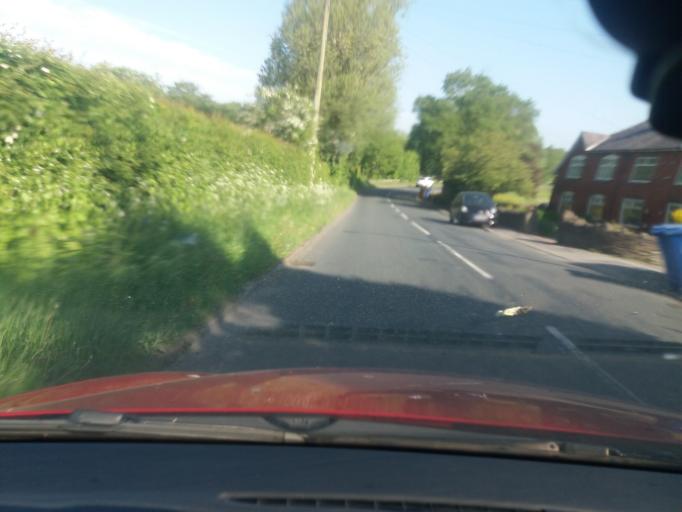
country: GB
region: England
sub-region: Borough of Wigan
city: Haigh
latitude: 53.6231
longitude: -2.5841
